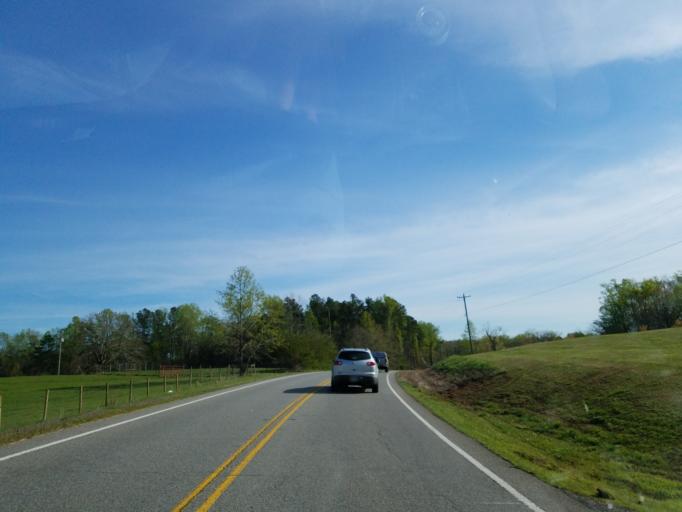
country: US
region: Georgia
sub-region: Dawson County
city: Dawsonville
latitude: 34.4529
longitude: -84.0879
